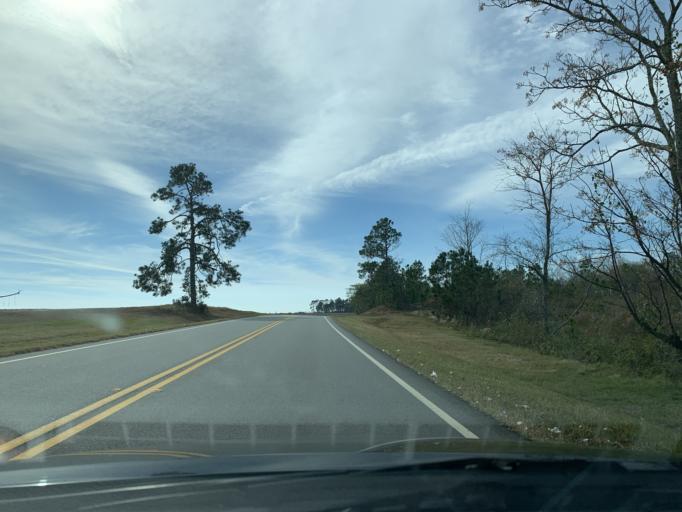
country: US
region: Georgia
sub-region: Turner County
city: Ashburn
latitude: 31.7869
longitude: -83.5071
